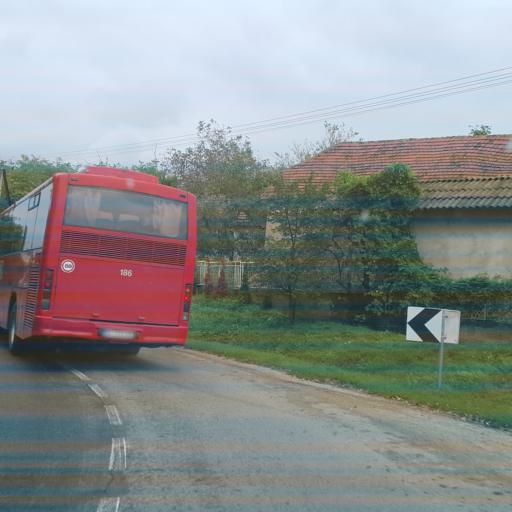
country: RS
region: Central Serbia
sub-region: Nisavski Okrug
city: Aleksinac
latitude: 43.5943
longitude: 21.6281
